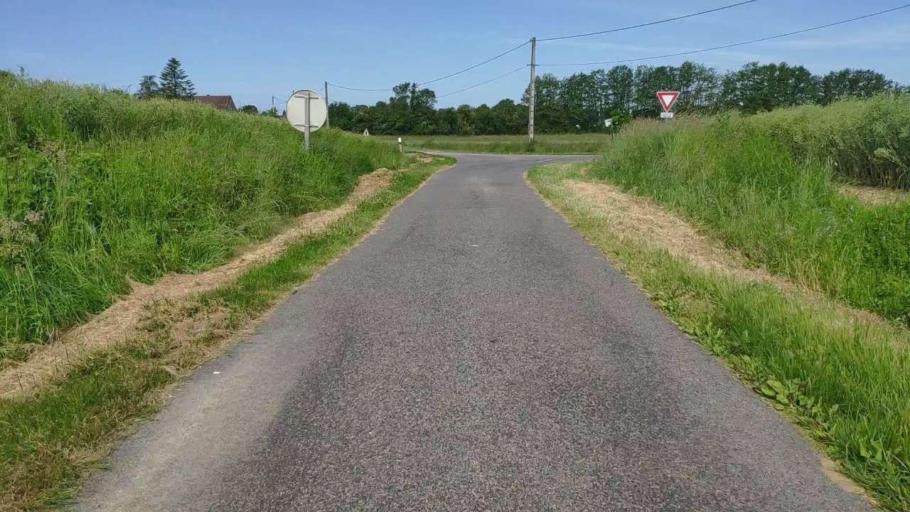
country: FR
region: Franche-Comte
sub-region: Departement du Jura
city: Bletterans
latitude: 46.6896
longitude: 5.4047
